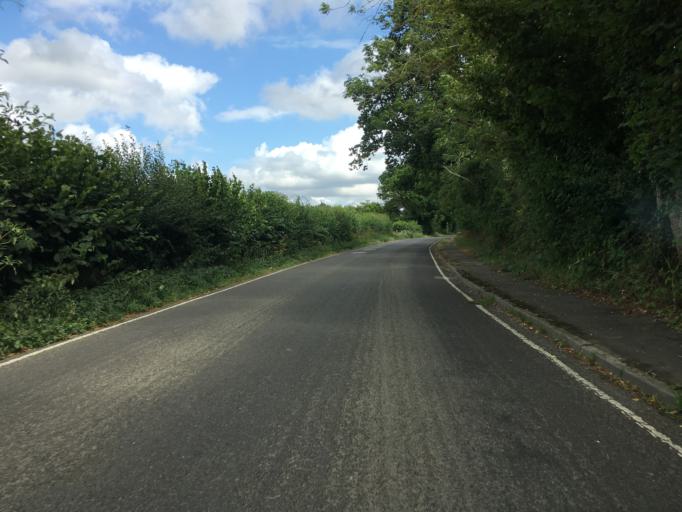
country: GB
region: England
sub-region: Kent
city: Staplehurst
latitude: 51.2232
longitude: 0.5760
